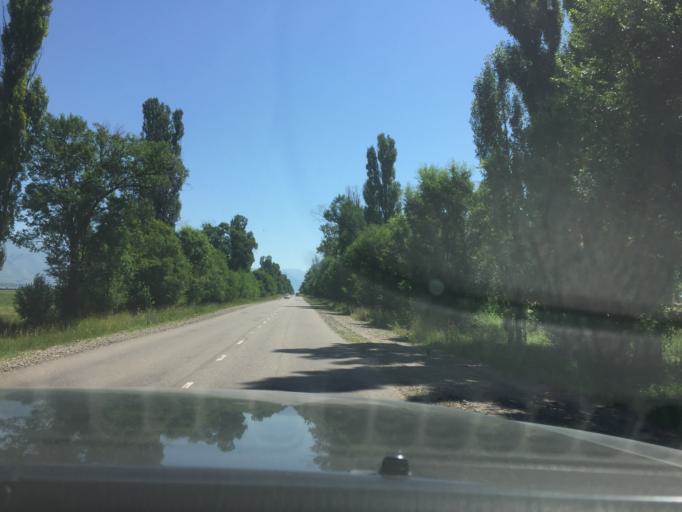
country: KG
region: Ysyk-Koel
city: Tyup
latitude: 42.7433
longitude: 78.4052
